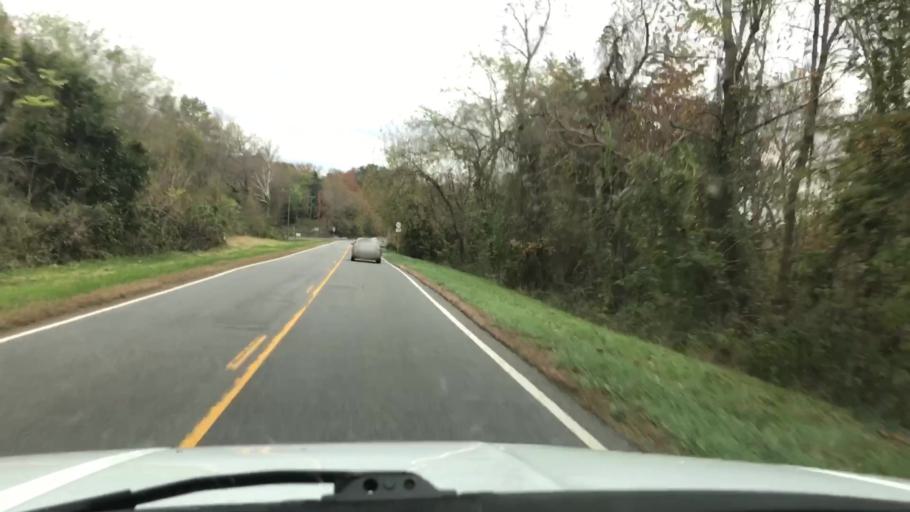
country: US
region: Virginia
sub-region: Goochland County
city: Goochland
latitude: 37.6167
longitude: -77.7561
